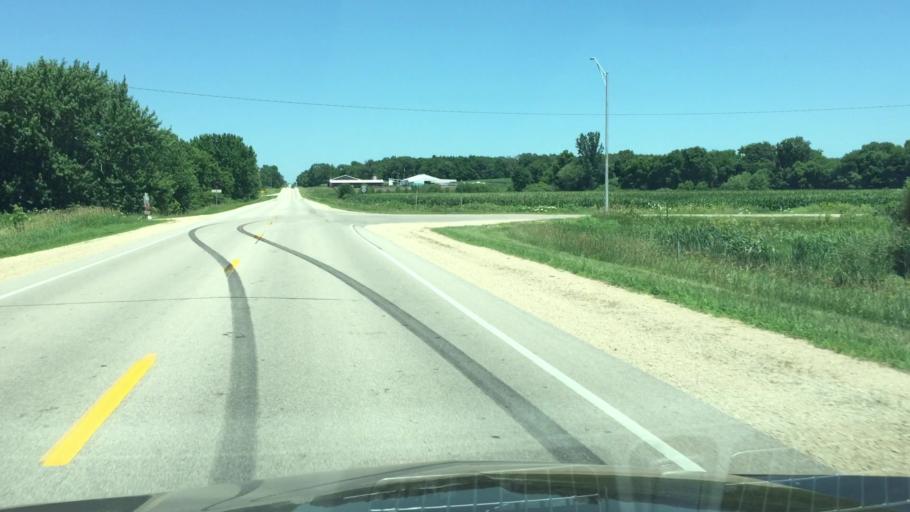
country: US
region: Iowa
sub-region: Cedar County
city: Mechanicsville
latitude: 42.0191
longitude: -91.1367
